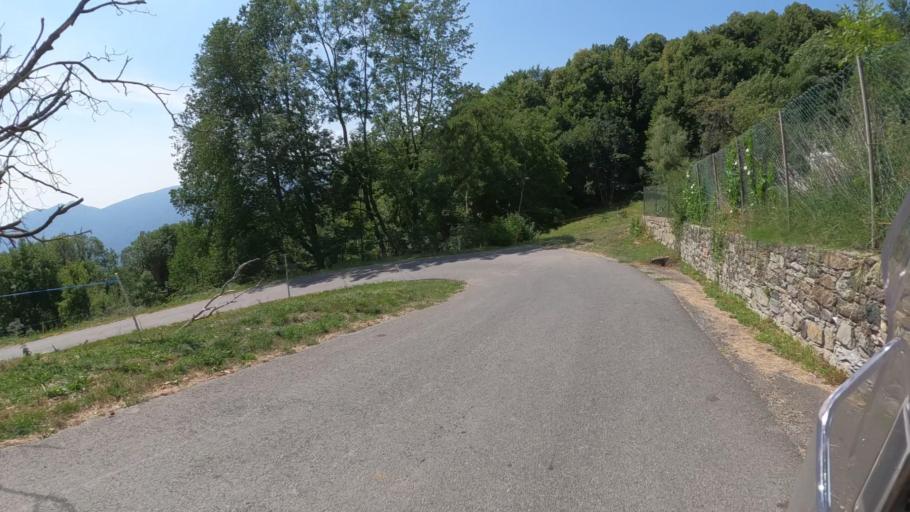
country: IT
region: Piedmont
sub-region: Provincia di Torino
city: Sant'Antonino di Susa
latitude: 45.1408
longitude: 7.2822
